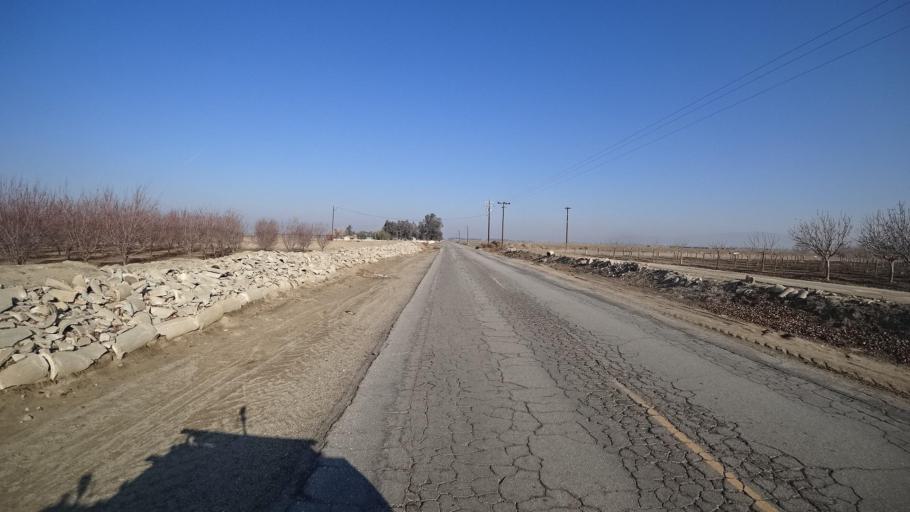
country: US
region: California
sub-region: Kern County
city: Weedpatch
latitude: 35.1504
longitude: -118.9677
